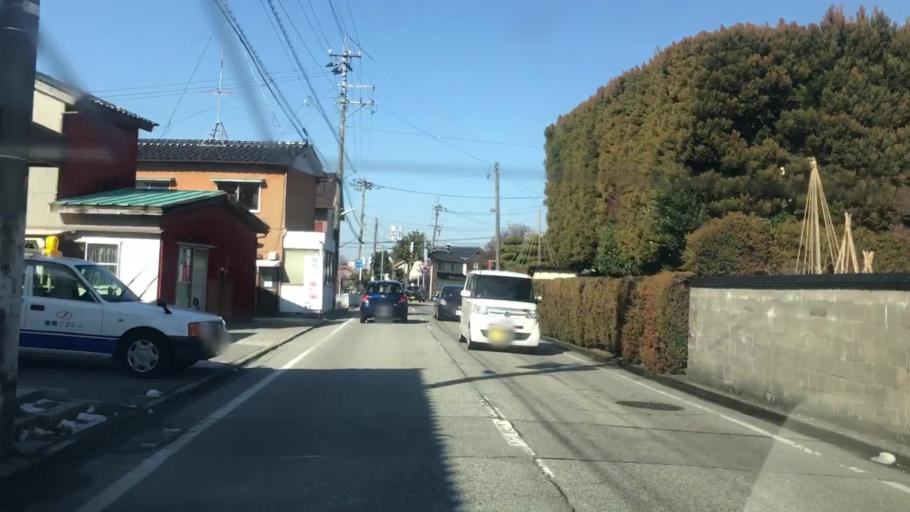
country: JP
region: Toyama
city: Toyama-shi
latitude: 36.6671
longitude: 137.2394
